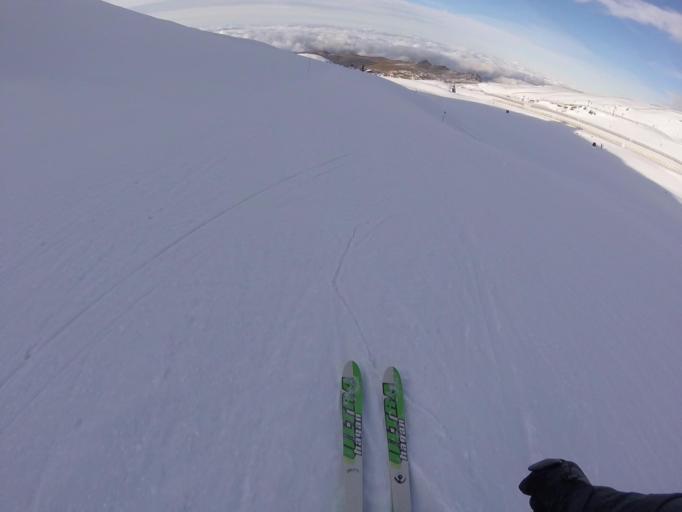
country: ES
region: Andalusia
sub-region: Provincia de Granada
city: Capileira
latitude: 37.0628
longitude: -3.3839
